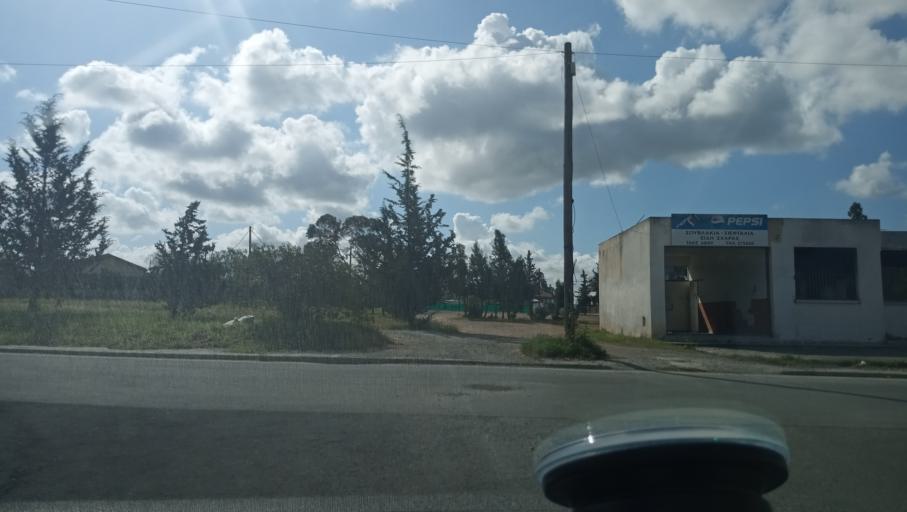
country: CY
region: Lefkosia
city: Geri
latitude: 35.1023
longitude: 33.4073
